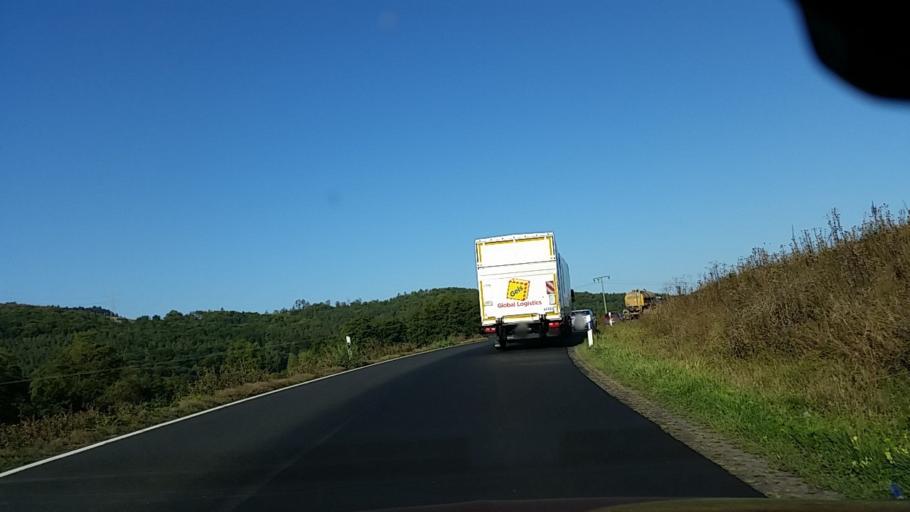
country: DE
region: Bavaria
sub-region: Regierungsbezirk Unterfranken
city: Gossenheim
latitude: 50.0084
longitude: 9.7956
